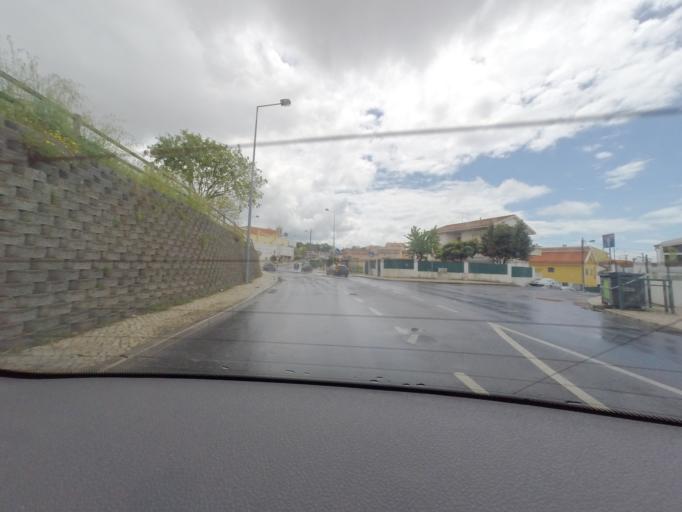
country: PT
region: Lisbon
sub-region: Cascais
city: Parede
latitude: 38.7036
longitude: -9.3431
